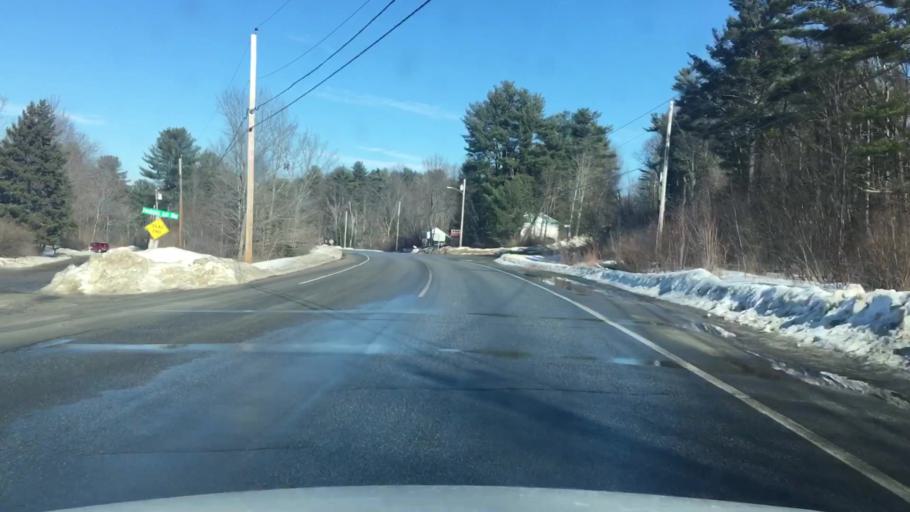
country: US
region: Maine
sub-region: Cumberland County
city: North Windham
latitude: 43.8313
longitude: -70.3826
